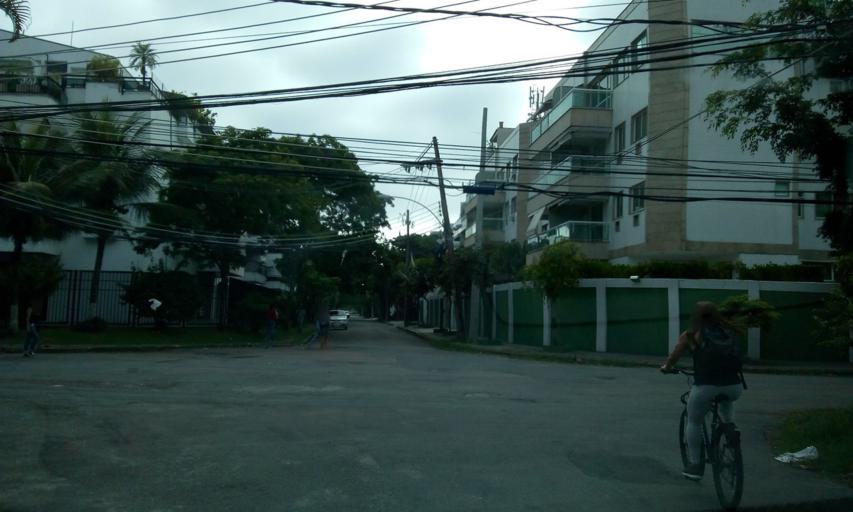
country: BR
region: Rio de Janeiro
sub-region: Nilopolis
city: Nilopolis
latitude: -23.0142
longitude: -43.4531
